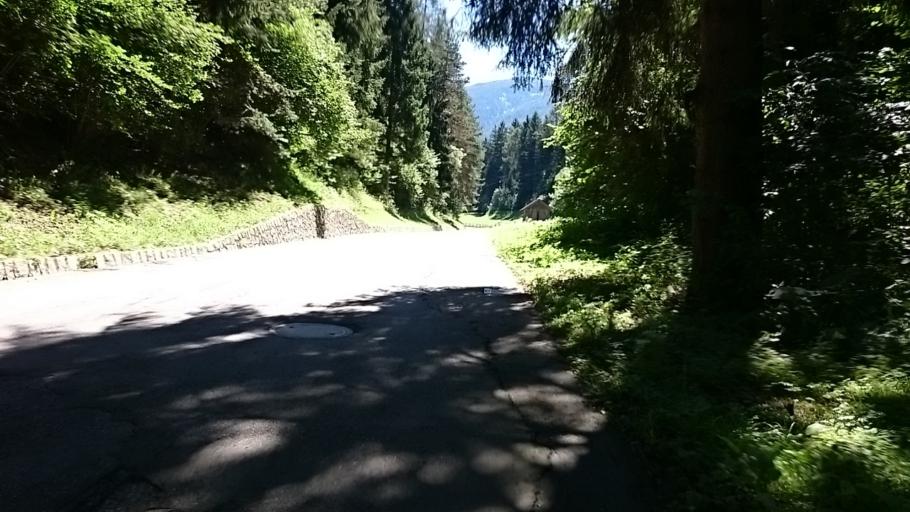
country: IT
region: Trentino-Alto Adige
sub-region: Bolzano
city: San Lorenzo di Sebato
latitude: 46.7821
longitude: 11.8765
